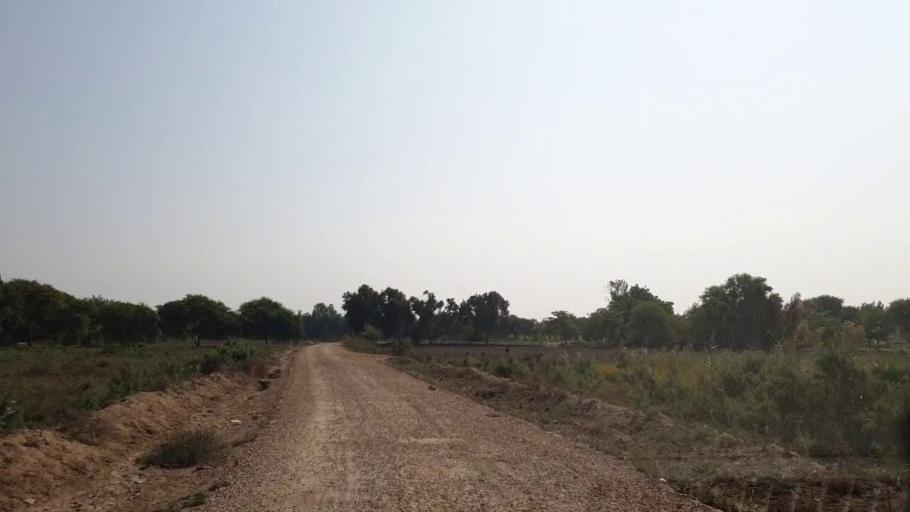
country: PK
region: Sindh
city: Tando Muhammad Khan
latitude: 25.0154
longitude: 68.4182
